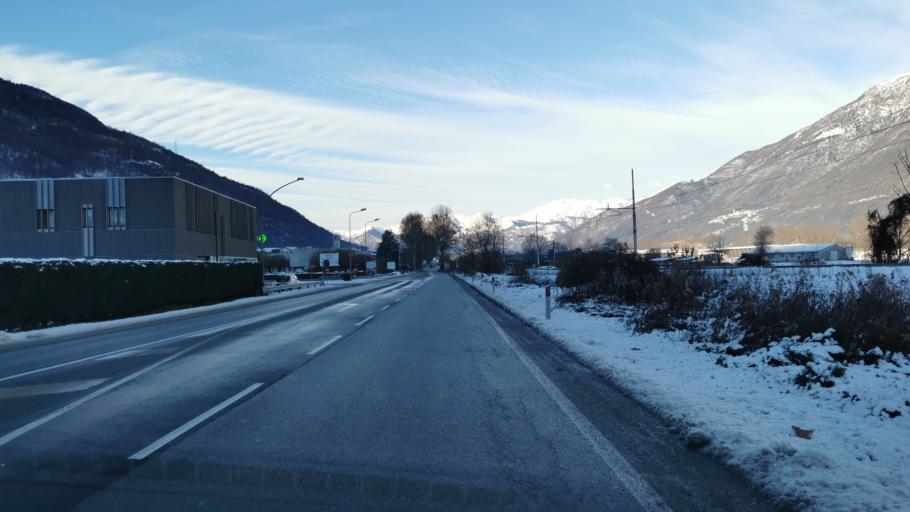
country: IT
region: Lombardy
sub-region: Provincia di Sondrio
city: Regoledo
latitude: 46.1338
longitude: 9.5412
